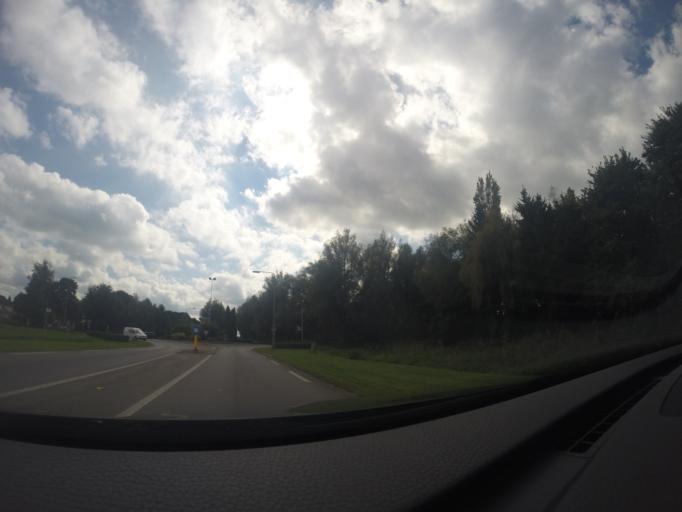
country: NL
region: Gelderland
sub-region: Gemeente Zevenaar
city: Zevenaar
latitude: 51.8655
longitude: 6.1091
